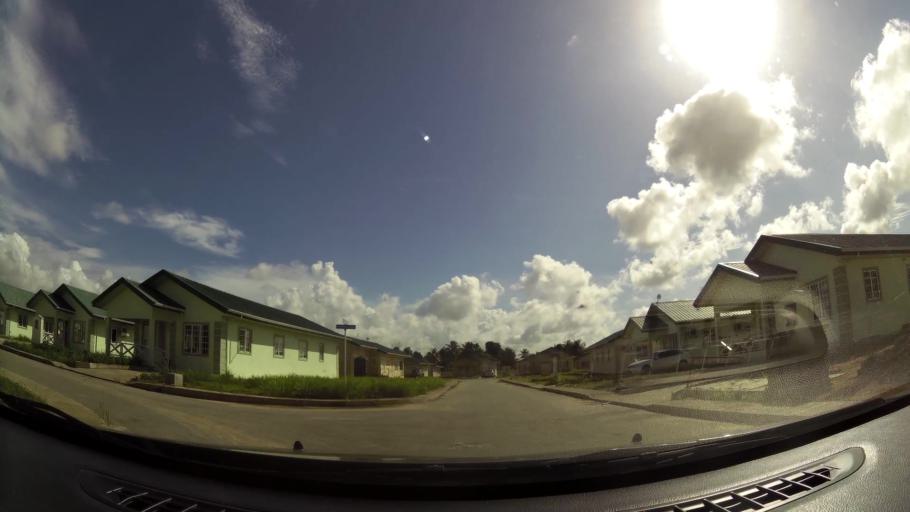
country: TT
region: Chaguanas
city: Chaguanas
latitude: 10.5327
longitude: -61.3926
